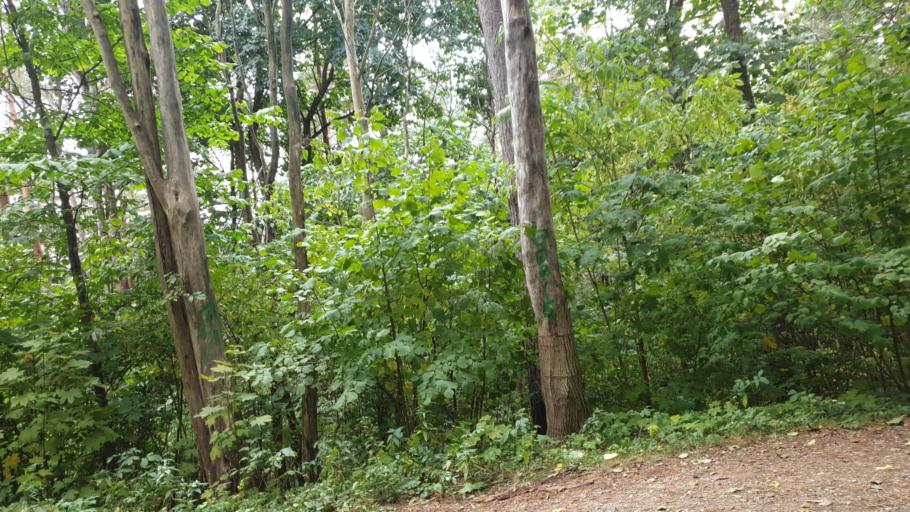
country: LT
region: Vilnius County
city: Seskine
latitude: 54.6933
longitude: 25.2320
